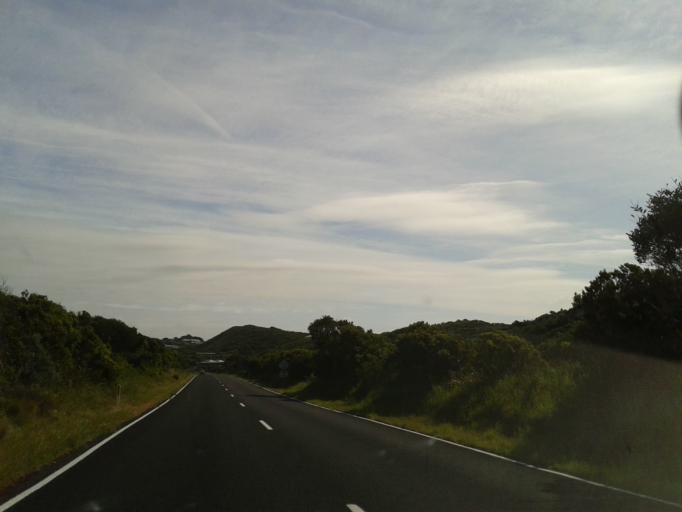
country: AU
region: Victoria
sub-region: Glenelg
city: Portland
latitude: -38.3649
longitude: 141.4133
